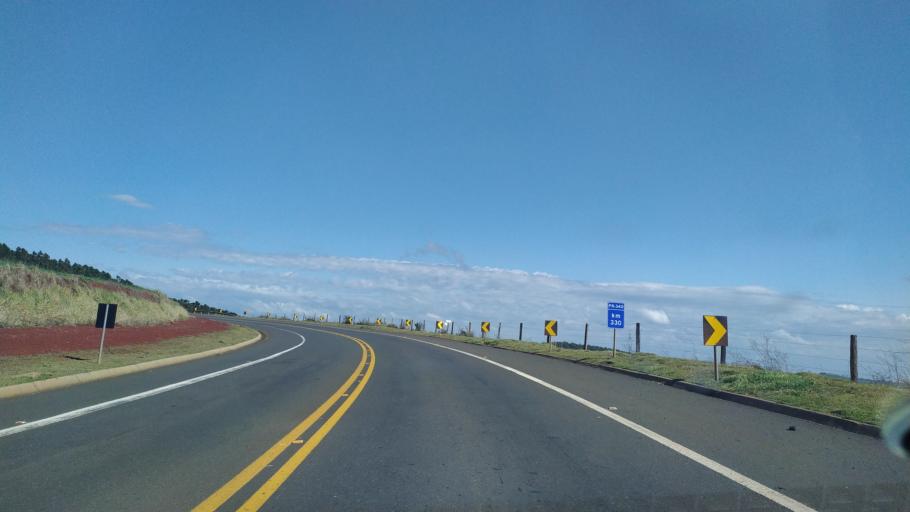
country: BR
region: Parana
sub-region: Ortigueira
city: Ortigueira
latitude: -24.2582
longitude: -50.8097
